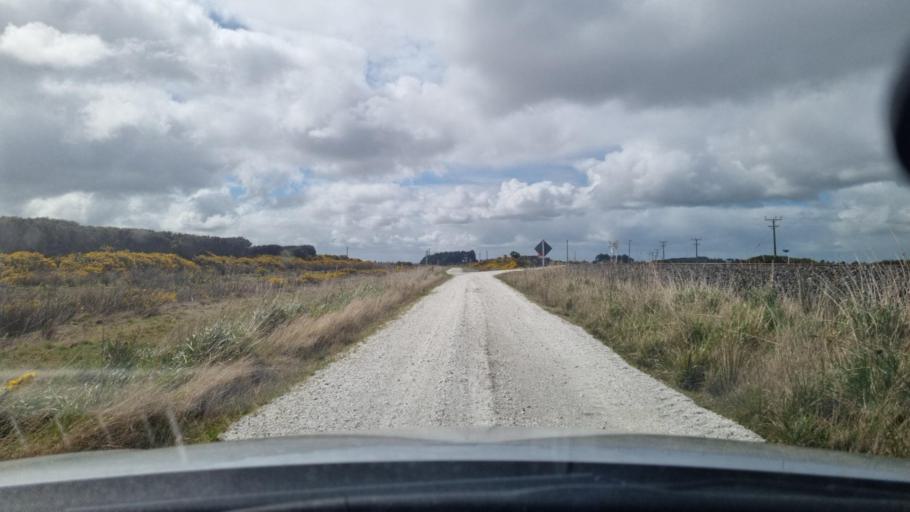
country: NZ
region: Southland
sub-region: Invercargill City
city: Bluff
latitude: -46.5283
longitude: 168.3066
